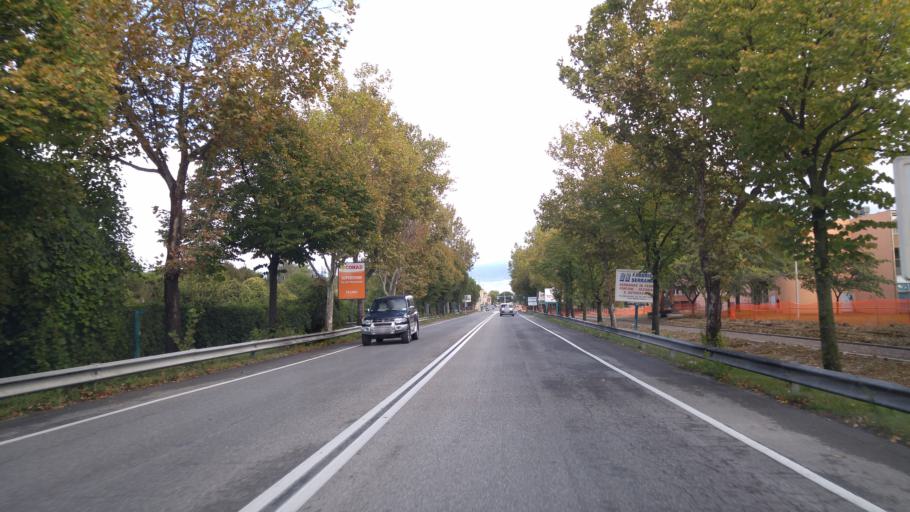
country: IT
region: The Marches
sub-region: Provincia di Pesaro e Urbino
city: Pesaro
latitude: 43.8942
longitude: 12.8919
